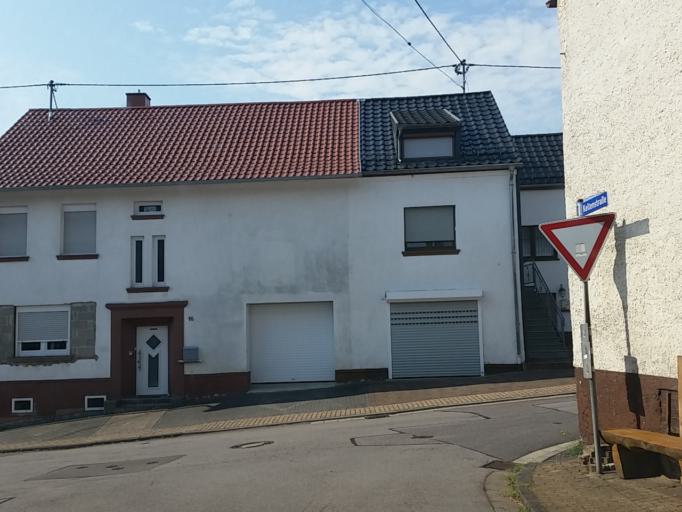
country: DE
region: Saarland
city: Wadern
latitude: 49.5076
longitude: 6.8676
